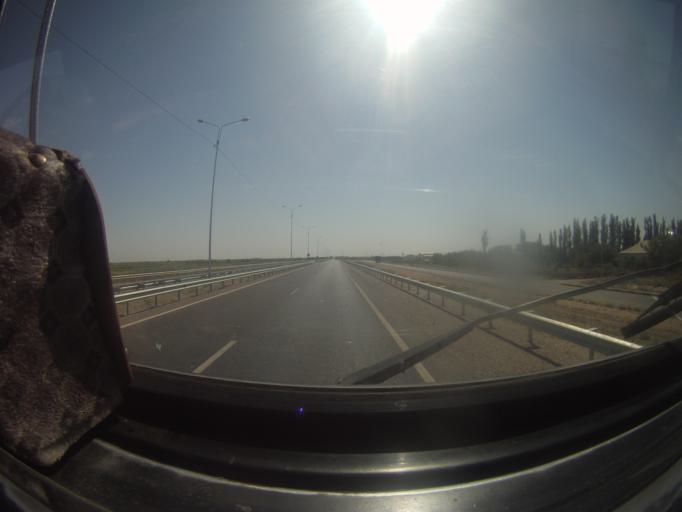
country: KZ
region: Ongtustik Qazaqstan
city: Turkestan
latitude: 43.3850
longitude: 68.0806
